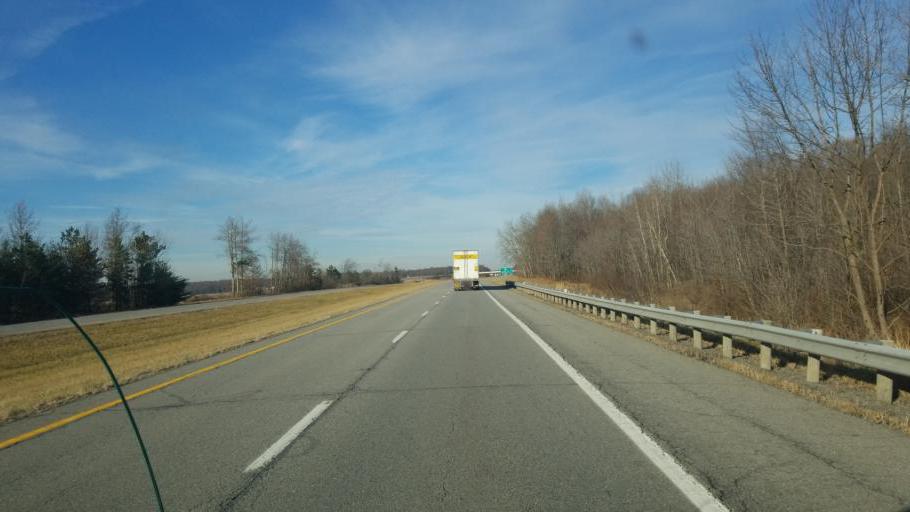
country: US
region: Ohio
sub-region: Trumbull County
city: Cortland
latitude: 41.4542
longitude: -80.7130
